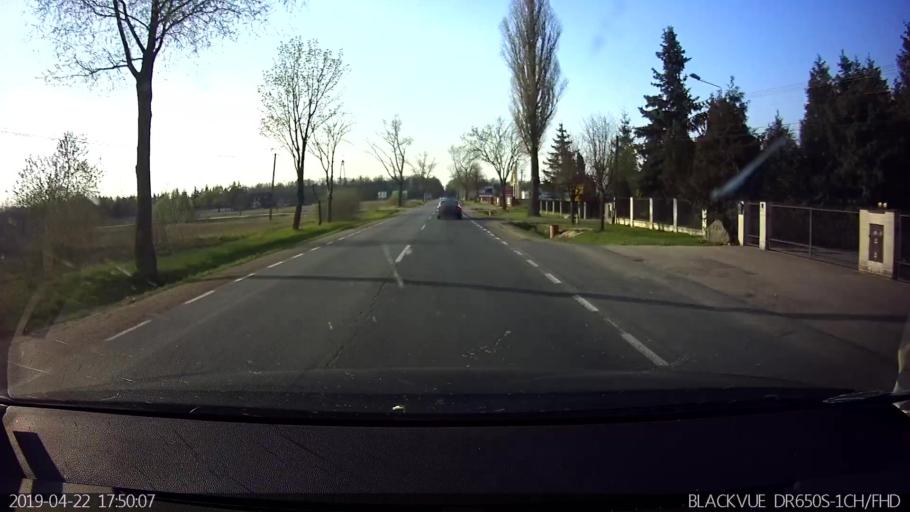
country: PL
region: Masovian Voivodeship
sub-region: Powiat wegrowski
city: Wegrow
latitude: 52.4208
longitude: 22.0043
